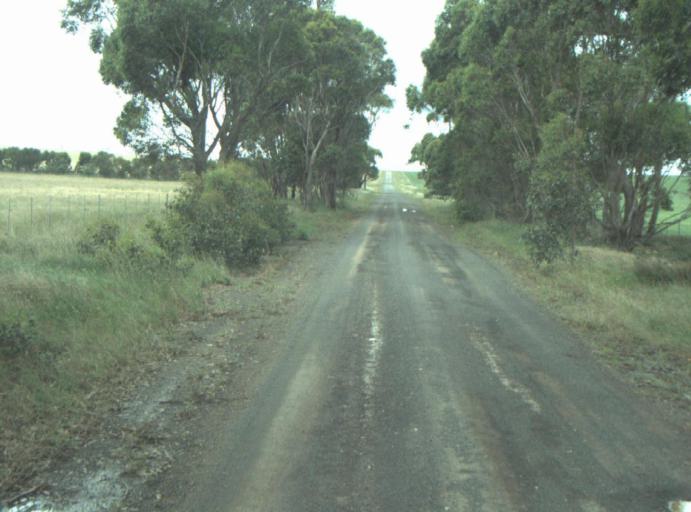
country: AU
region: Victoria
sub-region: Greater Geelong
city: Lara
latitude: -37.8819
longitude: 144.3502
